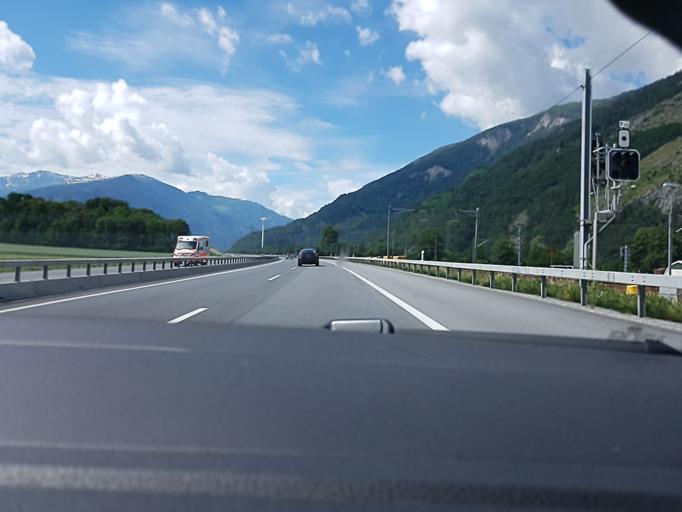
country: CH
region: Grisons
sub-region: Landquart District
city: Trimmis
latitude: 46.9069
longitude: 9.5504
